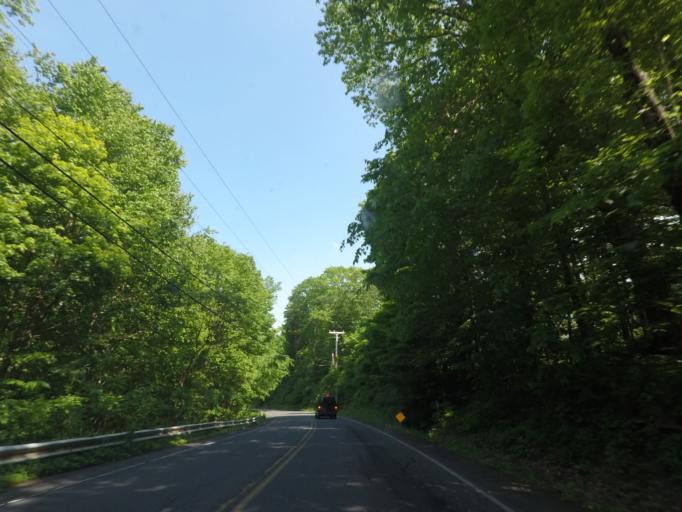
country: US
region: New York
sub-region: Dutchess County
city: Pine Plains
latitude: 41.9668
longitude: -73.5313
